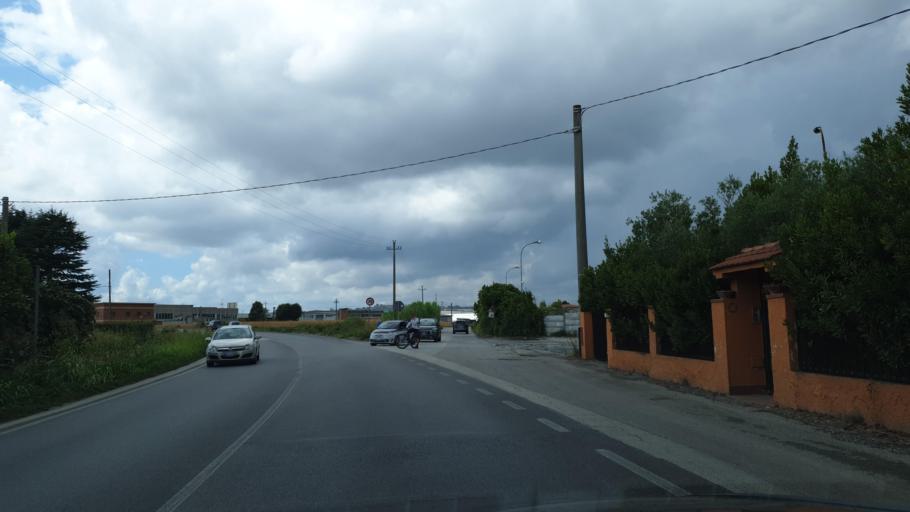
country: IT
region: Tuscany
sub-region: Provincia di Pistoia
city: Chiesina Uzzanese
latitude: 43.8465
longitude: 10.7315
